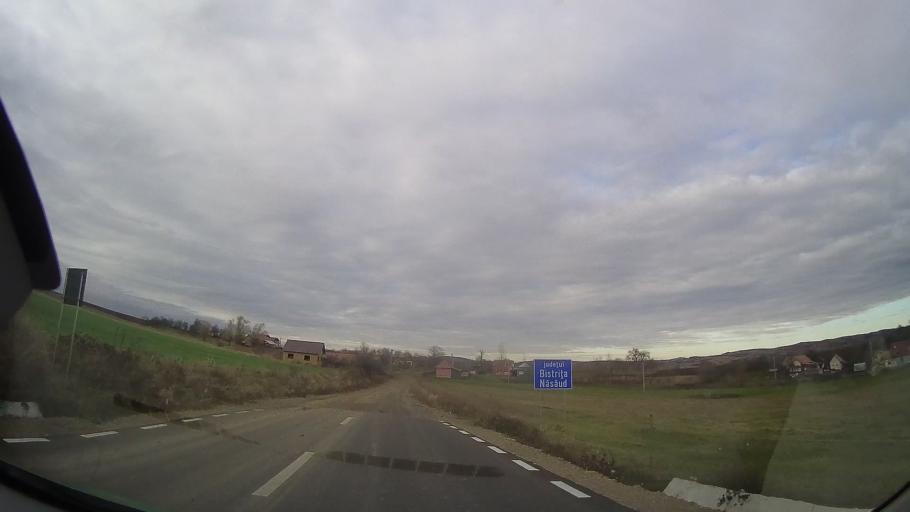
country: RO
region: Bistrita-Nasaud
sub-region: Comuna Milas
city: Milas
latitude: 46.8280
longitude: 24.4695
